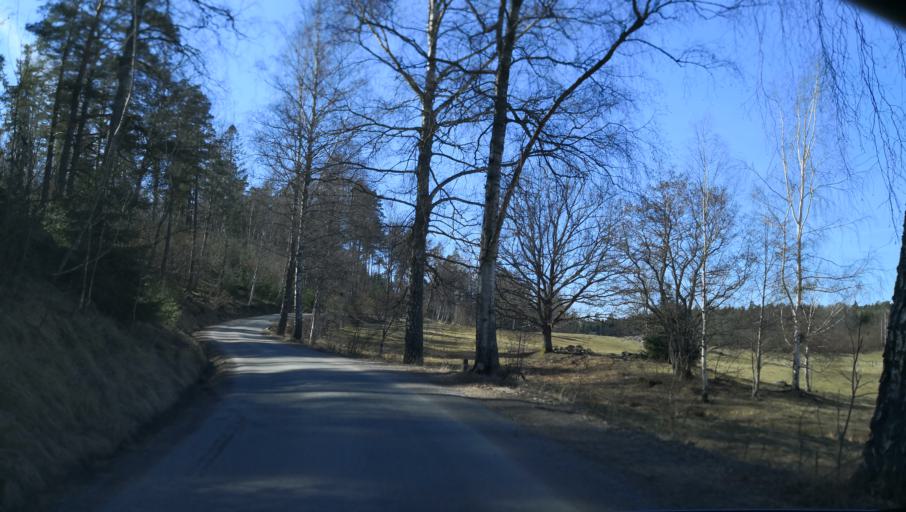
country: SE
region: Stockholm
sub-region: Varmdo Kommun
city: Gustavsberg
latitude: 59.2967
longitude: 18.4009
